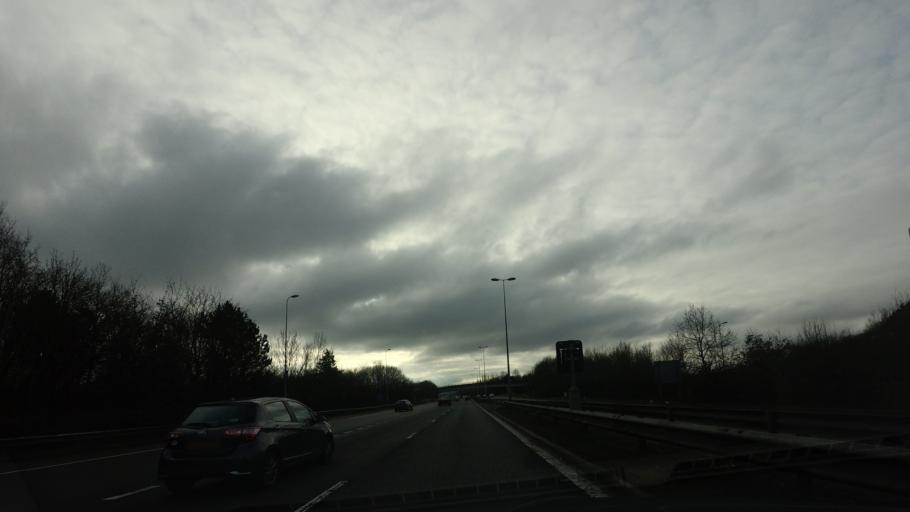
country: GB
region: England
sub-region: Kent
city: Halstead
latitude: 51.2928
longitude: 0.1436
